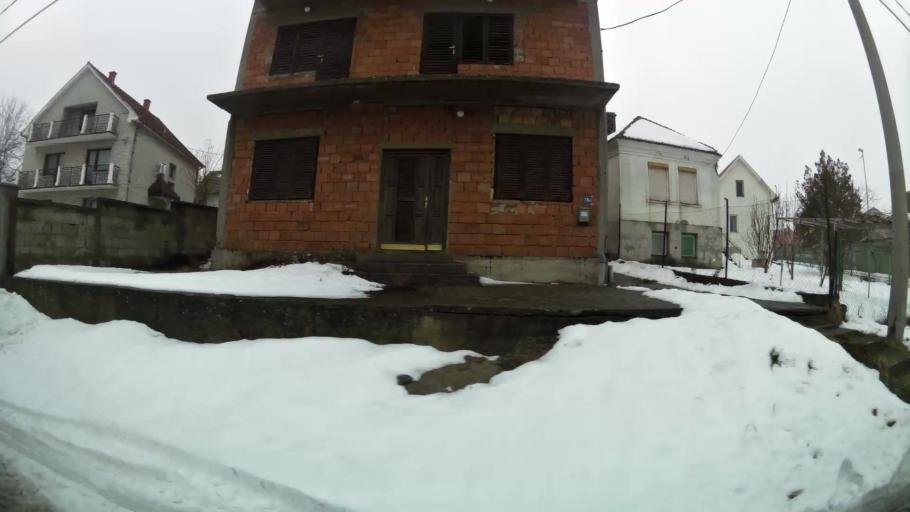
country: RS
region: Central Serbia
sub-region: Belgrade
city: Zvezdara
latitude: 44.7556
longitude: 20.5209
